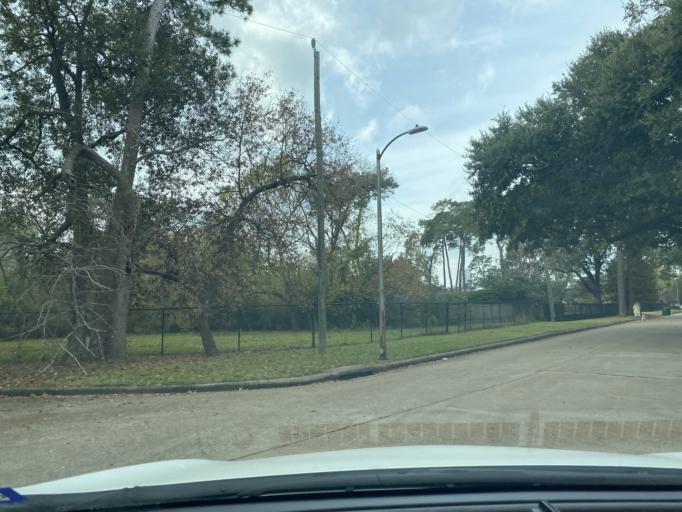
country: US
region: Texas
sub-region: Harris County
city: Hunters Creek Village
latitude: 29.7583
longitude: -95.4600
